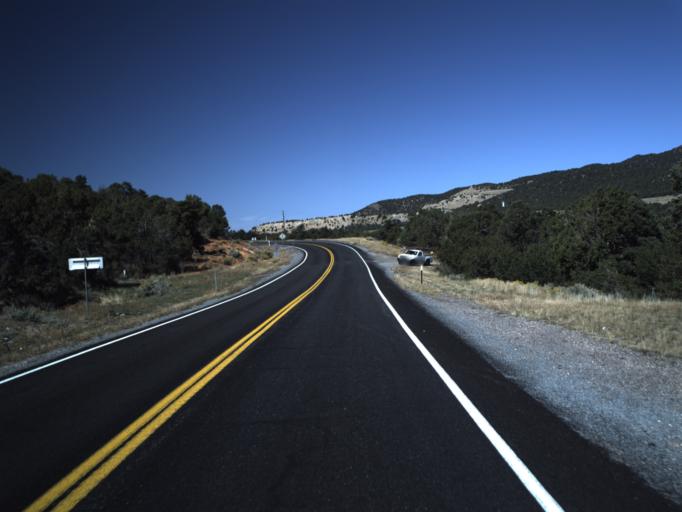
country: US
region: Utah
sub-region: Iron County
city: Cedar City
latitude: 37.6081
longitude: -113.3597
